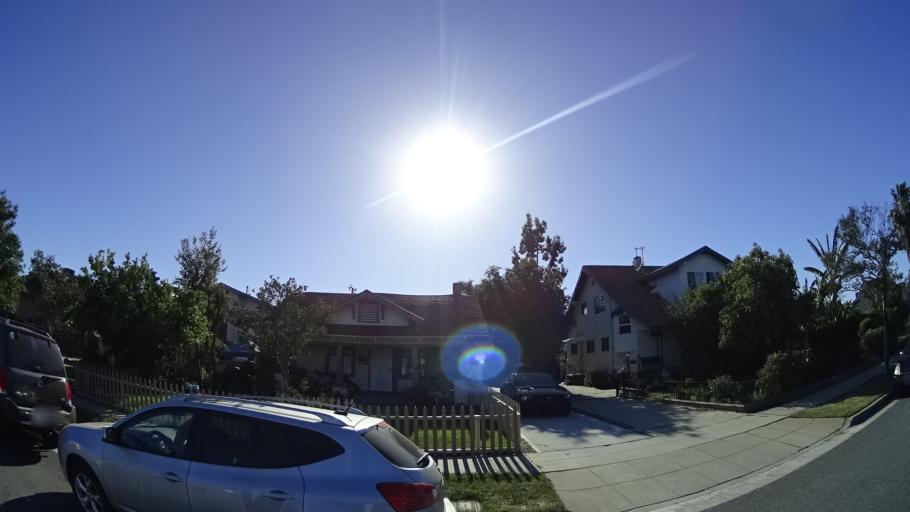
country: US
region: California
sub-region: Los Angeles County
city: Belvedere
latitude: 34.0678
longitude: -118.1559
